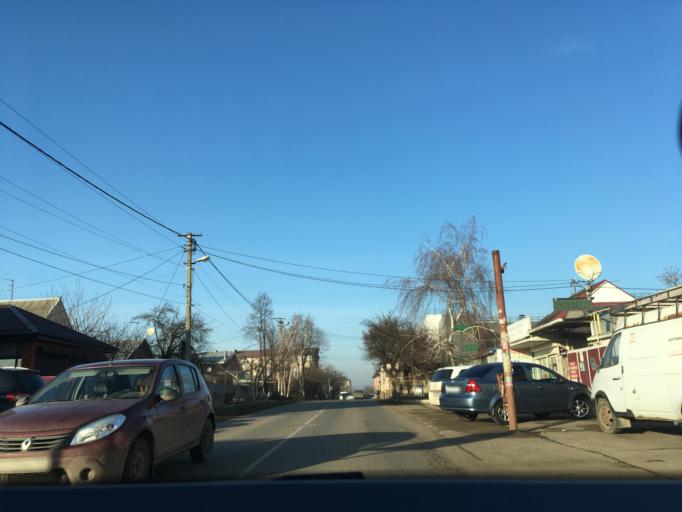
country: RU
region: Krasnodarskiy
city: Krasnodar
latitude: 45.0709
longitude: 39.0215
